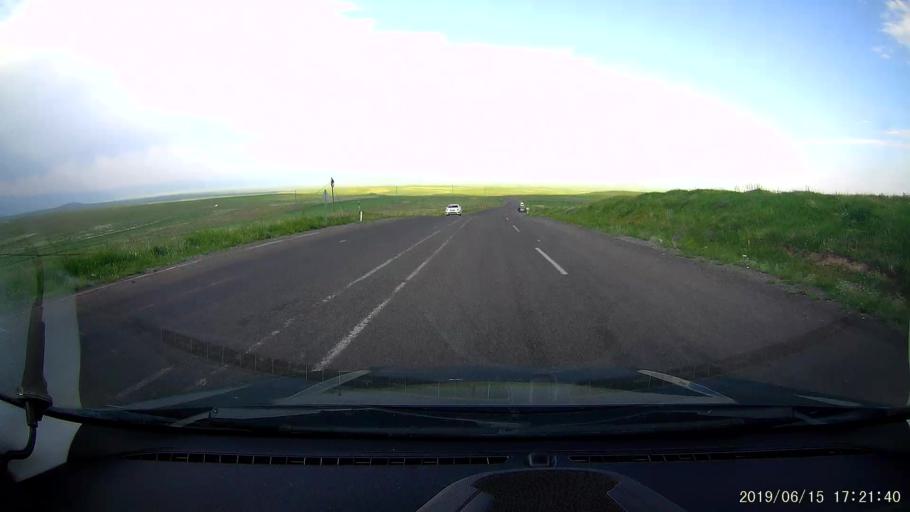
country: TR
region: Kars
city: Basgedikler
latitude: 40.6169
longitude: 43.3289
